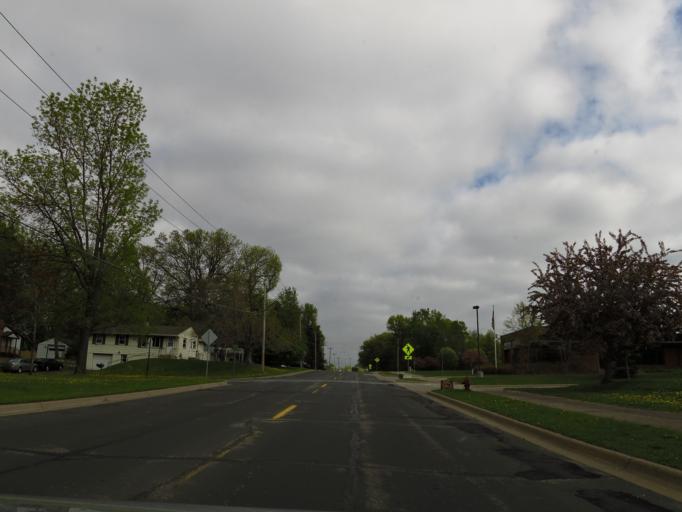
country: US
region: Minnesota
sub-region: Ramsey County
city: Maplewood
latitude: 44.9389
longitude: -92.9793
